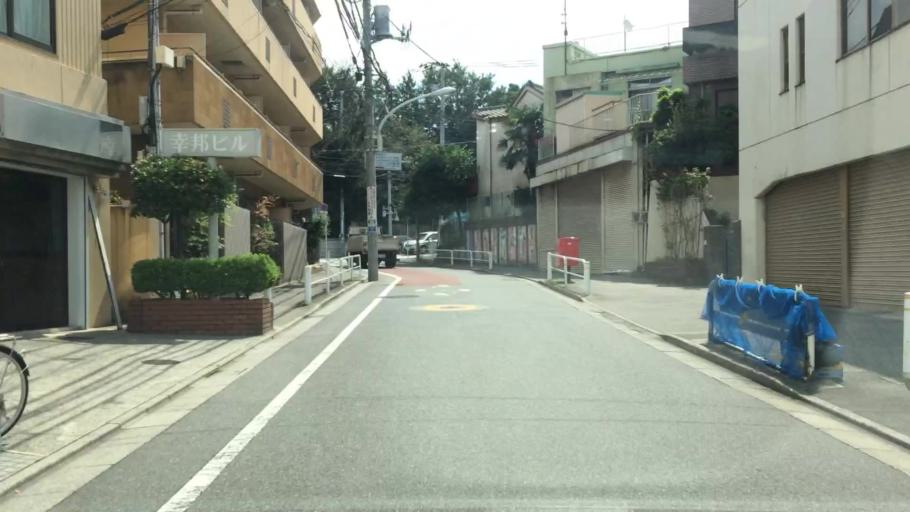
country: JP
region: Tokyo
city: Tokyo
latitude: 35.7468
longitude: 139.6874
